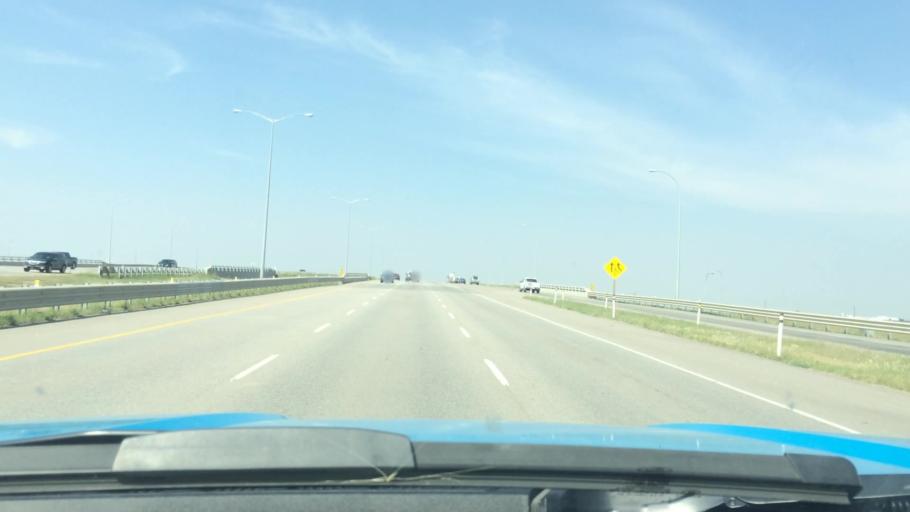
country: CA
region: Alberta
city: Chestermere
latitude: 50.9463
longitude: -113.9202
